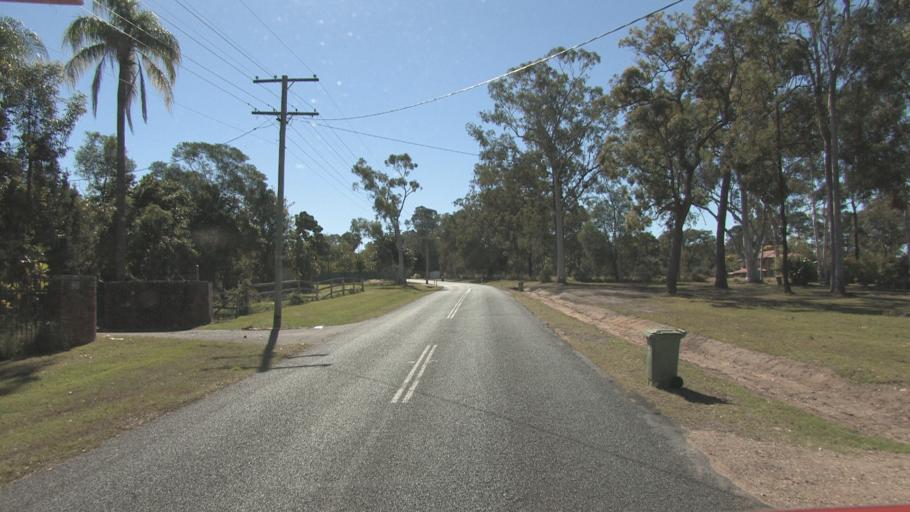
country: AU
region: Queensland
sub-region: Logan
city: Park Ridge South
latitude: -27.7118
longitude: 153.0586
